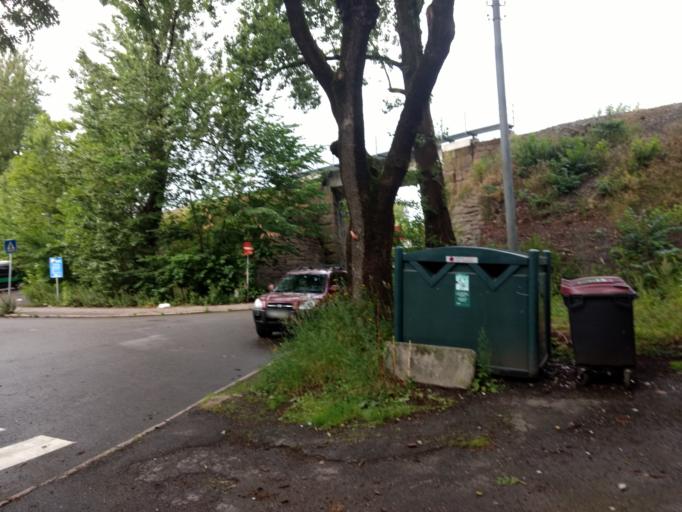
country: NO
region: Oslo
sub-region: Oslo
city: Oslo
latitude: 59.9328
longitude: 10.7830
